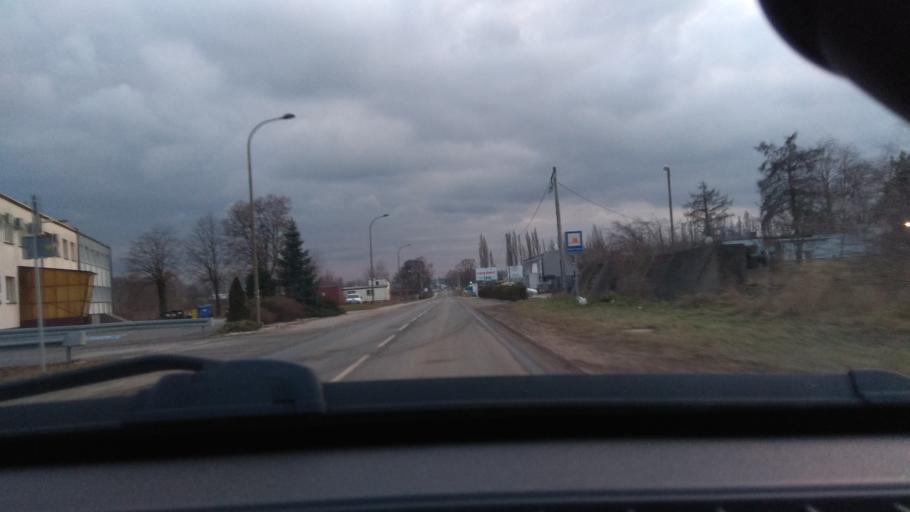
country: PL
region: Greater Poland Voivodeship
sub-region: Powiat kepinski
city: Kepno
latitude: 51.2968
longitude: 18.0061
